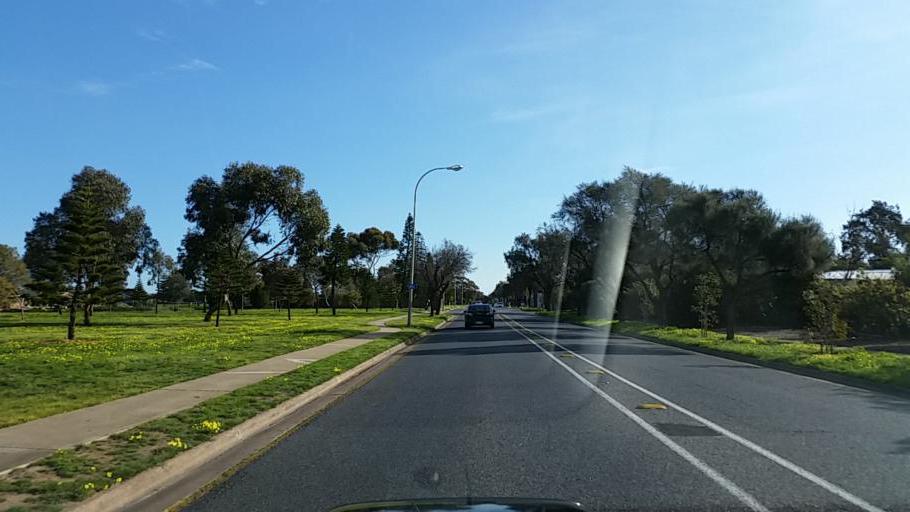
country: AU
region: South Australia
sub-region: Charles Sturt
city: West Lakes Shore
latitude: -34.8590
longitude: 138.4929
